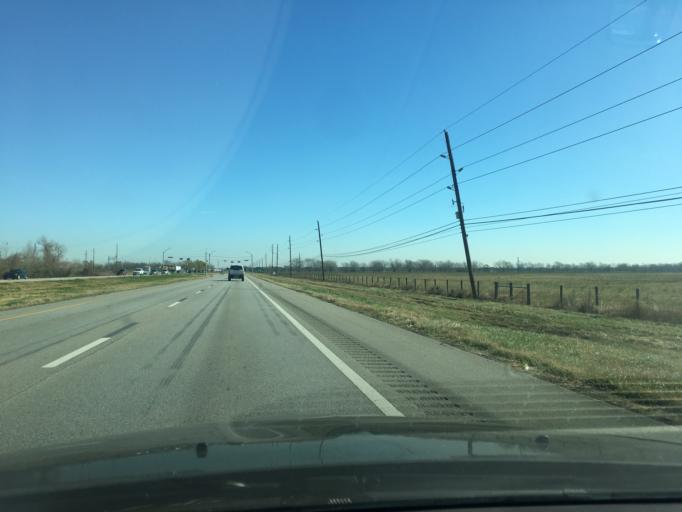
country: US
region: Texas
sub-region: Fort Bend County
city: Pecan Grove
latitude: 29.5982
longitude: -95.7169
